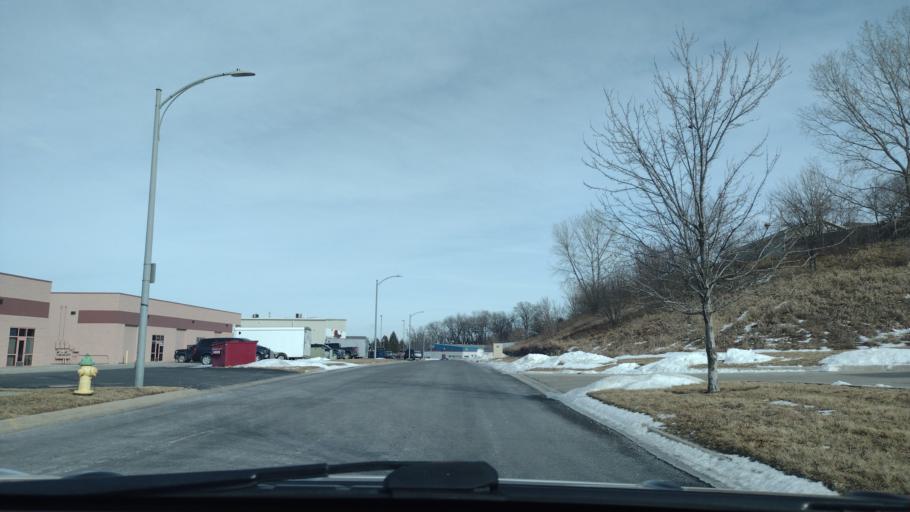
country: US
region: Nebraska
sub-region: Sarpy County
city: Papillion
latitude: 41.1410
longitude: -96.0267
